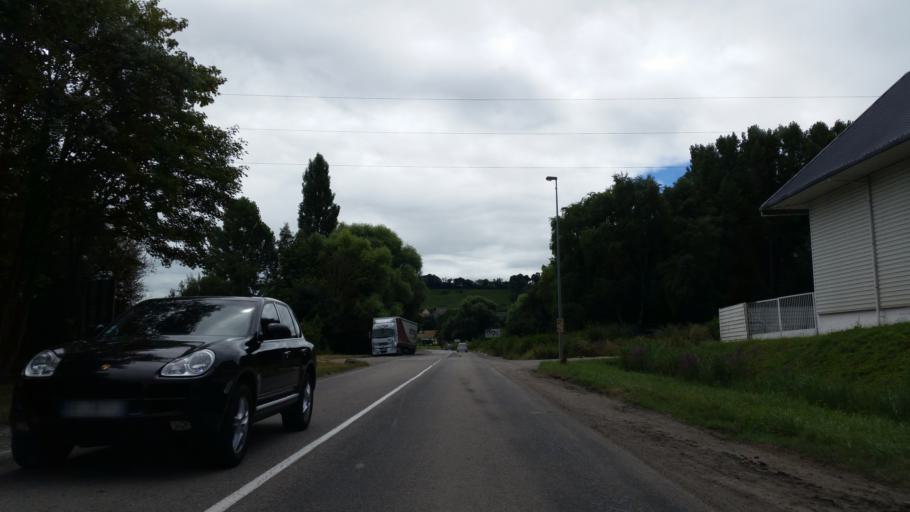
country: FR
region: Lower Normandy
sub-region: Departement du Calvados
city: La Riviere-Saint-Sauveur
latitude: 49.4144
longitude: 0.2591
